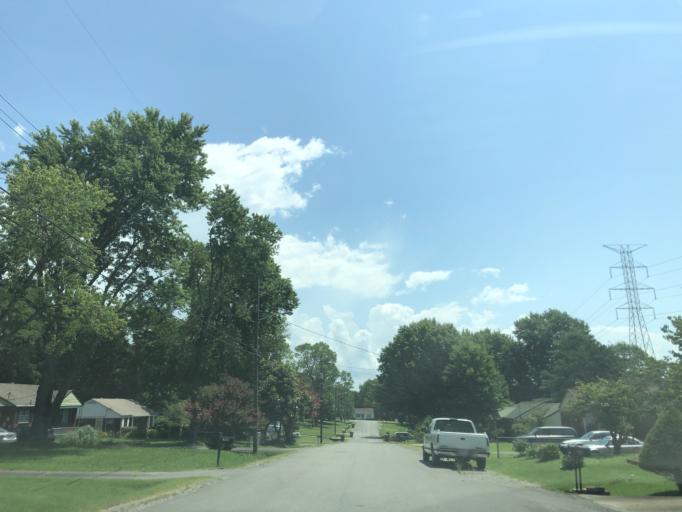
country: US
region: Tennessee
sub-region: Davidson County
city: Lakewood
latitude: 36.1576
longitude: -86.6562
